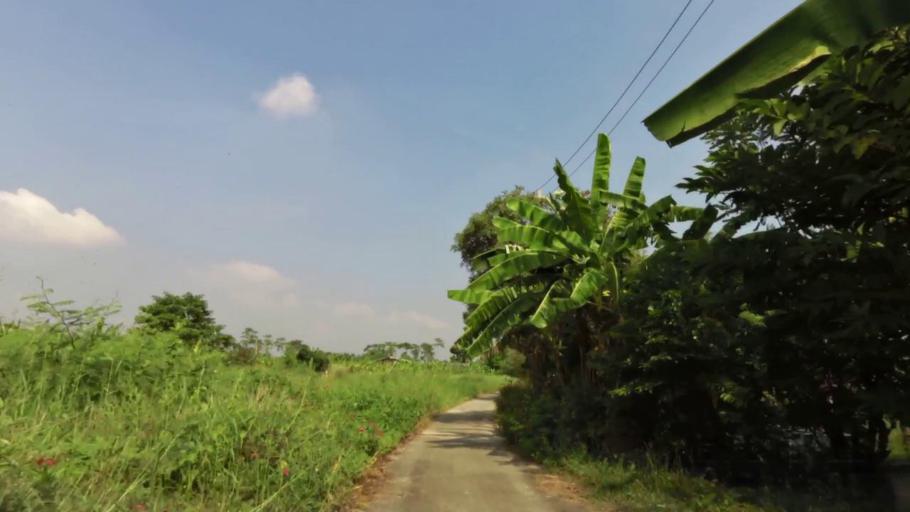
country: TH
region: Ang Thong
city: Wiset Chaichan
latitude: 14.6087
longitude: 100.3922
